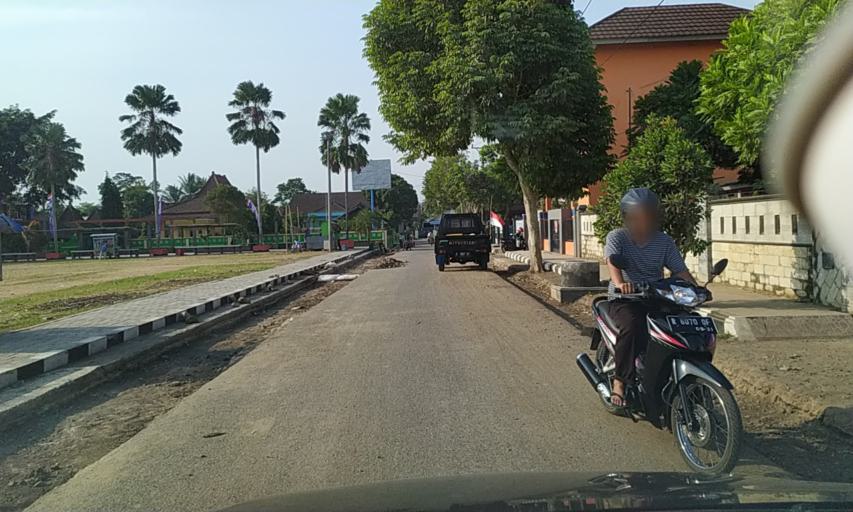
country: ID
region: Central Java
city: Sidareja
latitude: -7.4836
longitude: 108.7917
